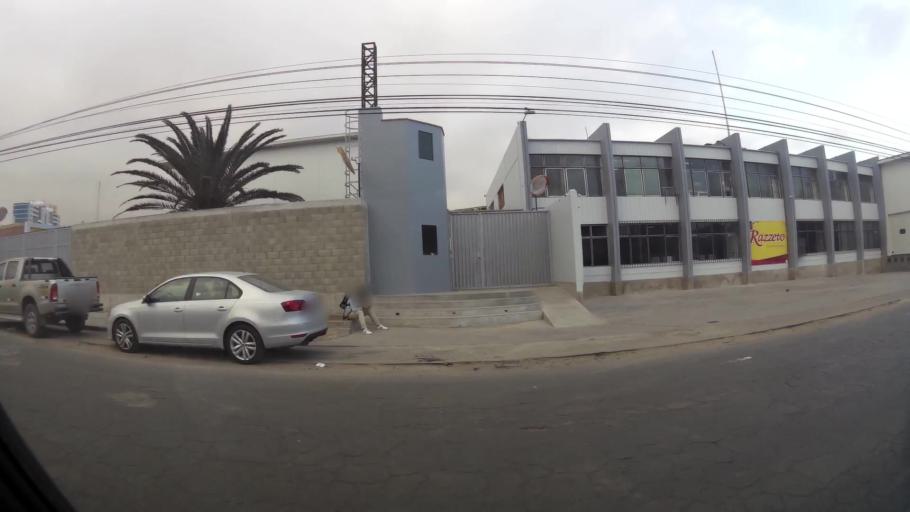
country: PE
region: La Libertad
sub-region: Provincia de Trujillo
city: La Esperanza
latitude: -8.0940
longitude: -79.0333
